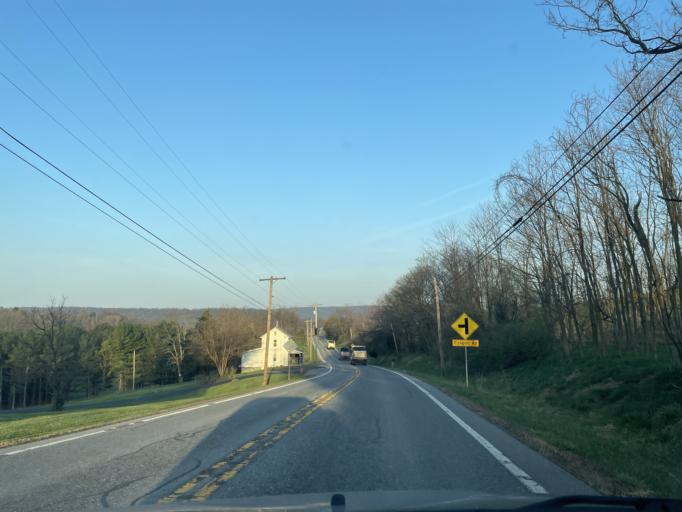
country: US
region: Maryland
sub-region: Washington County
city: Hancock
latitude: 39.6983
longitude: -78.2081
